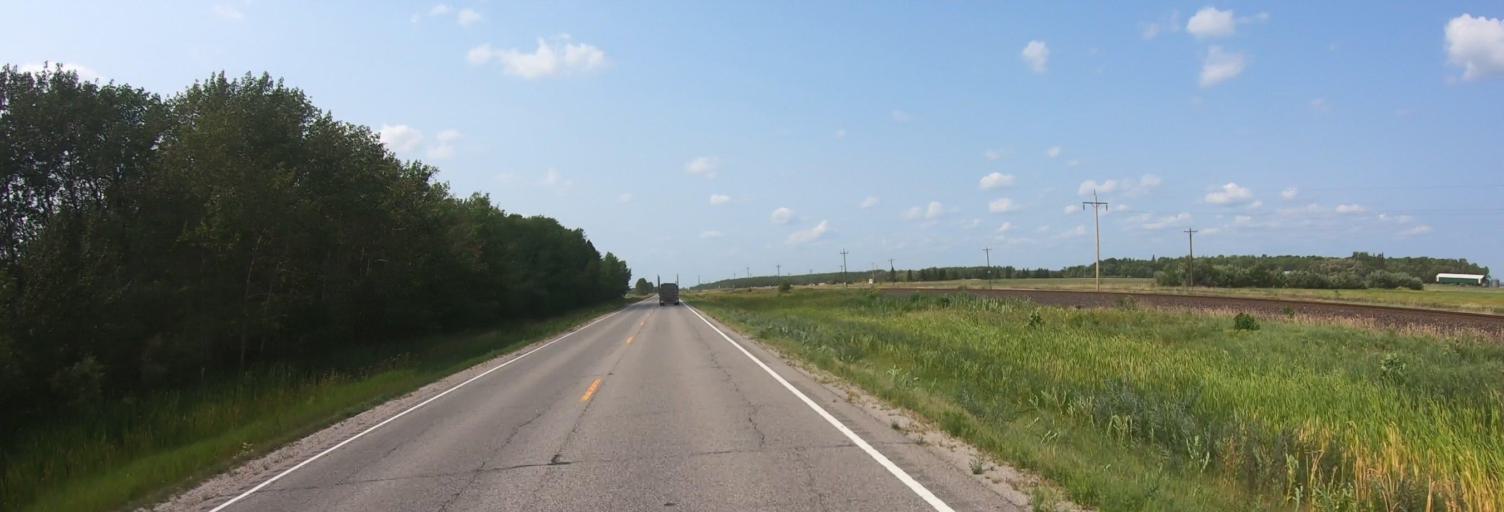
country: US
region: Minnesota
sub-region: Roseau County
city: Warroad
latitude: 48.8595
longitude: -95.2374
